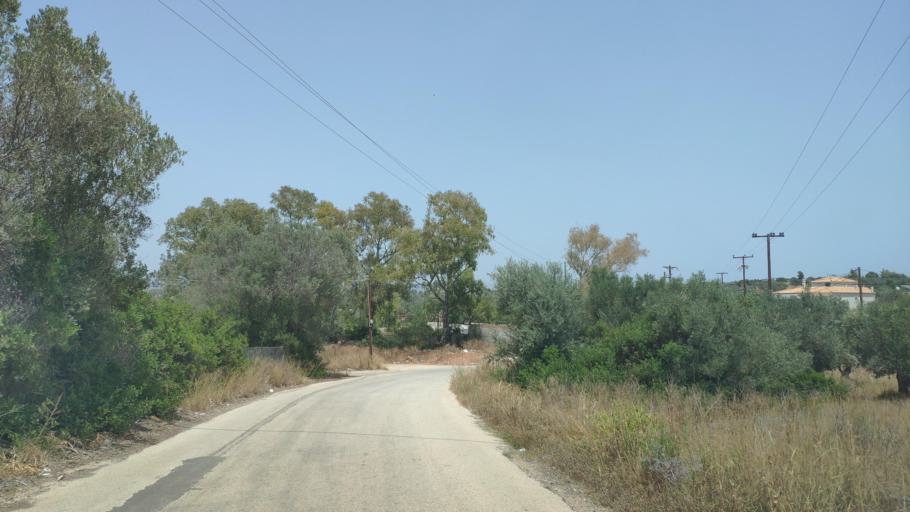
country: GR
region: Peloponnese
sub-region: Nomos Argolidos
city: Porto Cheli
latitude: 37.3106
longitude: 23.1573
